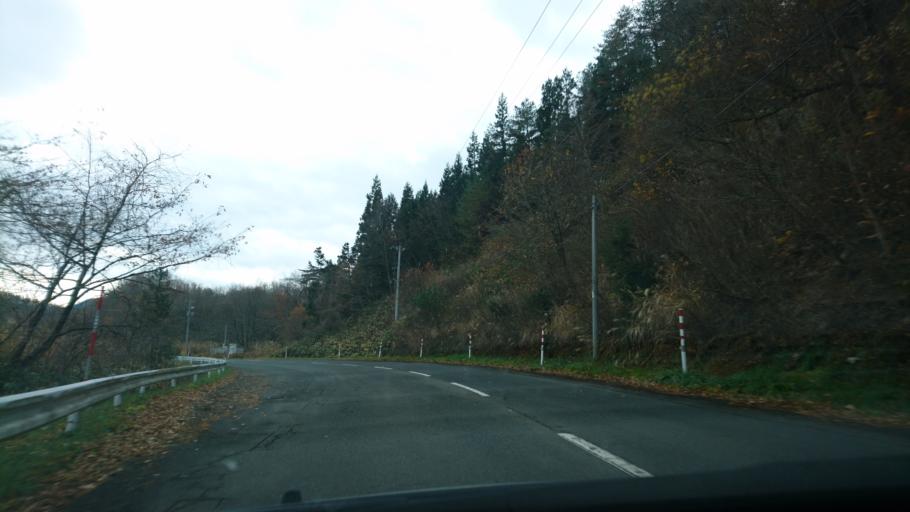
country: JP
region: Iwate
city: Ichinoseki
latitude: 38.9302
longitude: 140.9221
